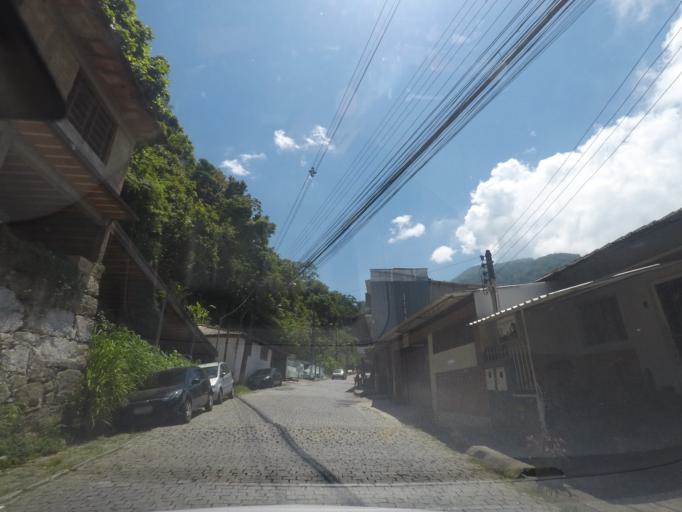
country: BR
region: Rio de Janeiro
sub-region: Petropolis
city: Petropolis
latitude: -22.5351
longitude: -43.1717
